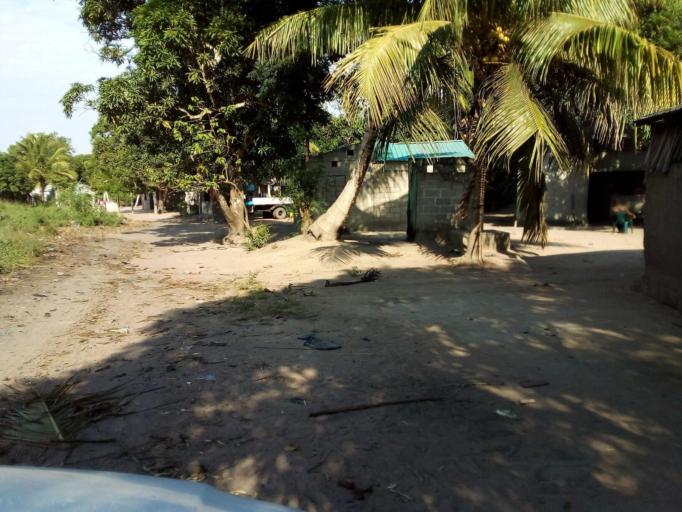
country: MZ
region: Zambezia
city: Quelimane
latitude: -17.6151
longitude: 36.8228
